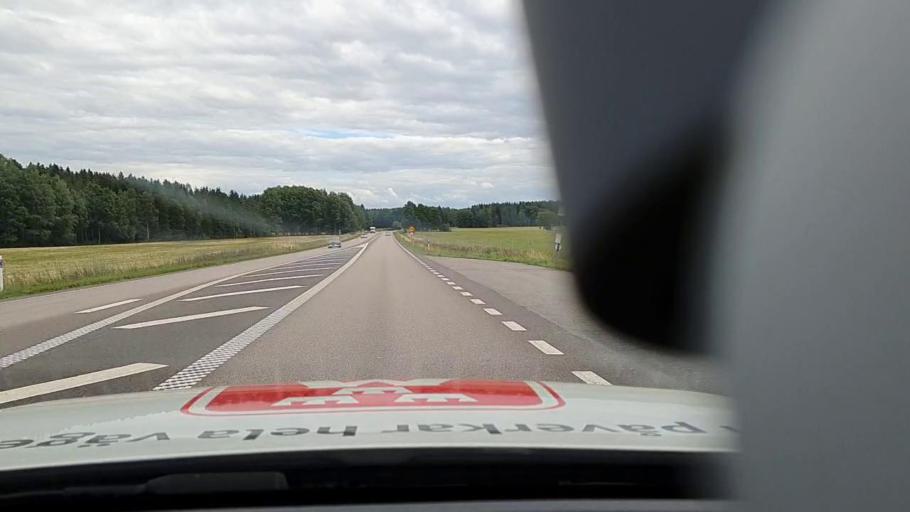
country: SE
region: Vaestra Goetaland
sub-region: Lidkopings Kommun
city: Vinninga
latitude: 58.4392
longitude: 13.2692
